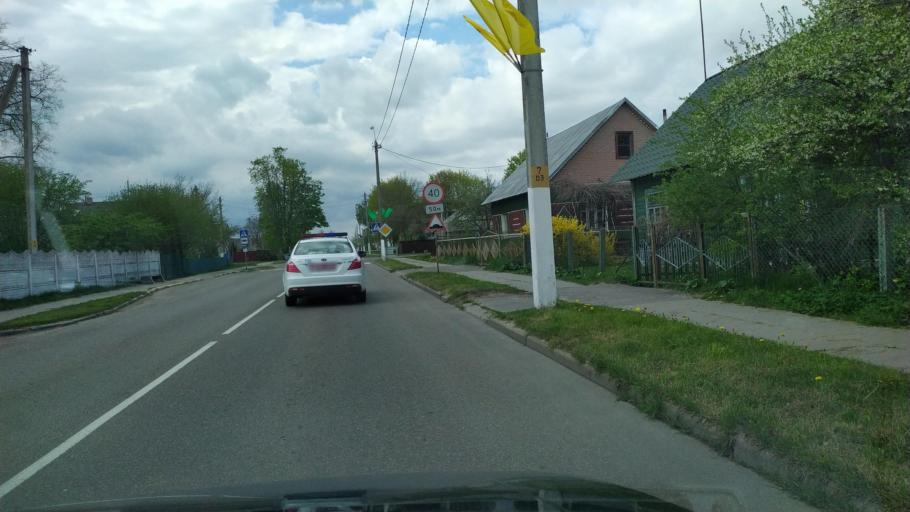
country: BY
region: Brest
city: Pruzhany
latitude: 52.5576
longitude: 24.4327
